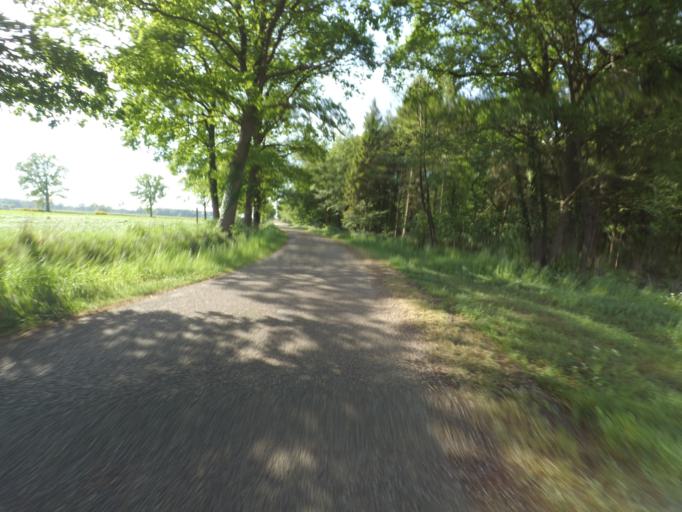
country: NL
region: Overijssel
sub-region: Gemeente Oldenzaal
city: Oldenzaal
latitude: 52.3659
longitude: 6.9770
